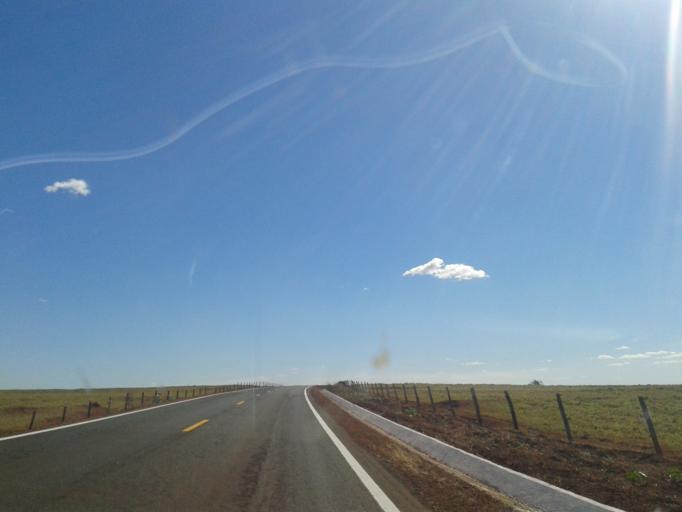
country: BR
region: Minas Gerais
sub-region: Capinopolis
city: Capinopolis
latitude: -18.6916
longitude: -49.5001
